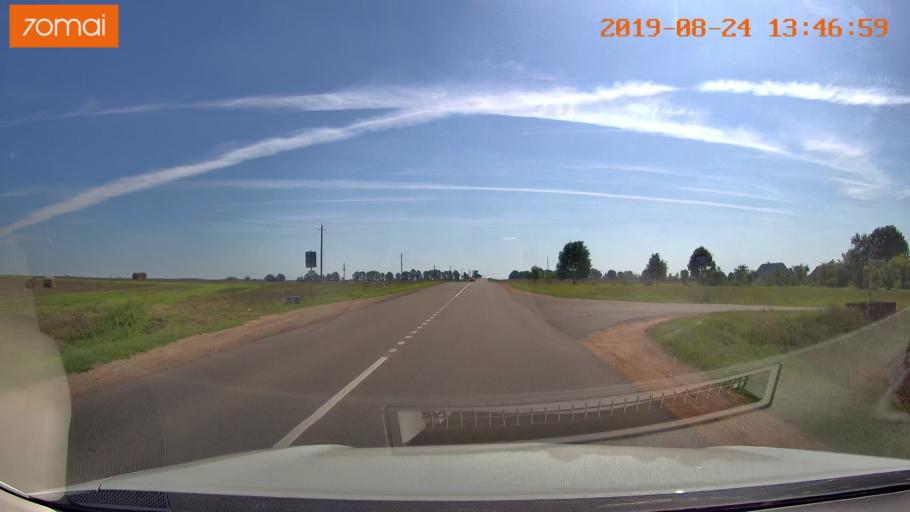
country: BY
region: Minsk
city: Samakhvalavichy
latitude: 53.6678
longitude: 27.5367
